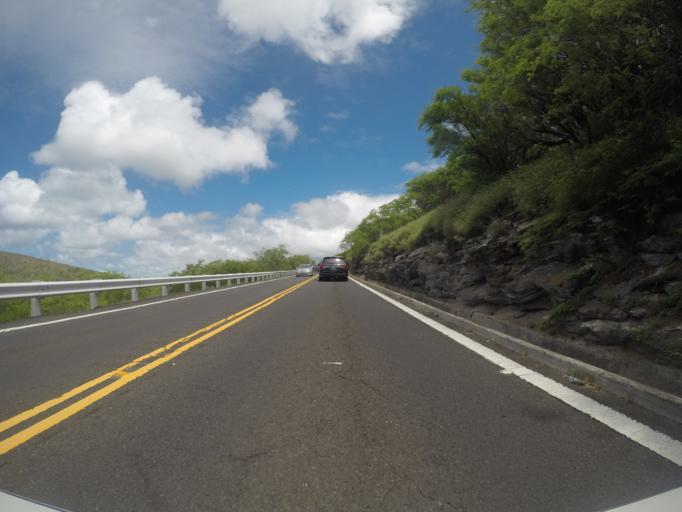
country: US
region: Hawaii
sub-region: Honolulu County
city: Waimanalo Beach
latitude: 21.2734
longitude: -157.6898
